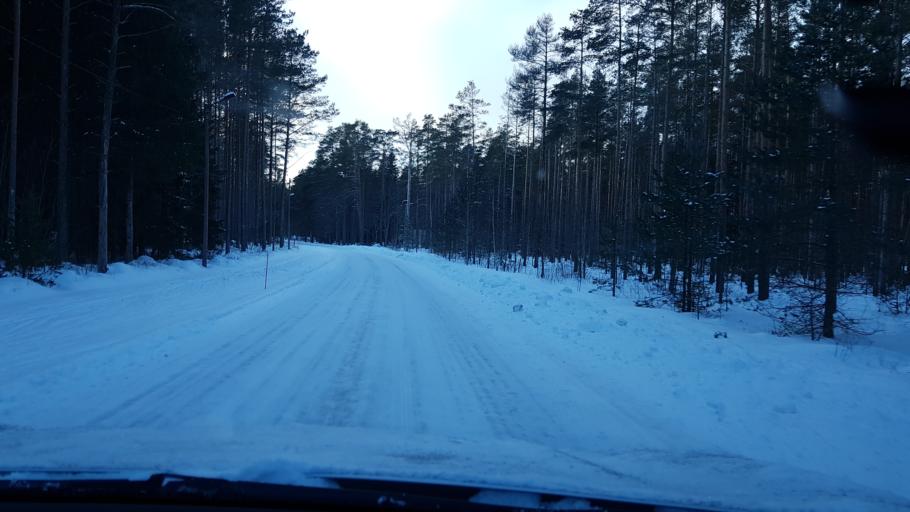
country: EE
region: Harju
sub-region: Nissi vald
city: Turba
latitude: 59.2238
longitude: 24.1509
